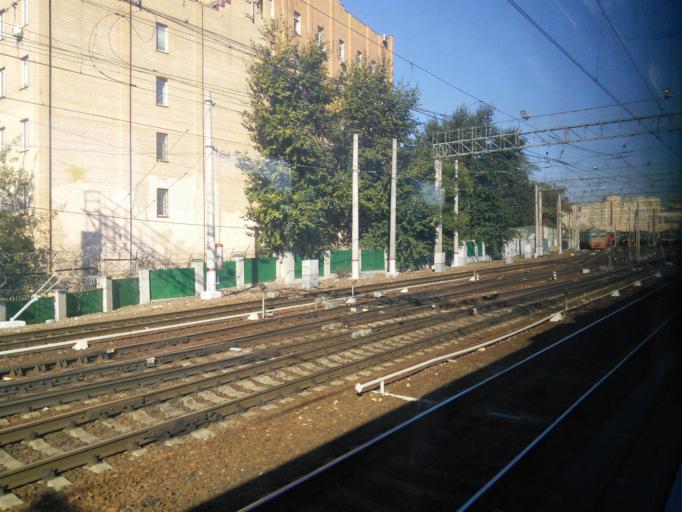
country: RU
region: Moscow
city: Taganskiy
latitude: 55.7532
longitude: 37.6661
